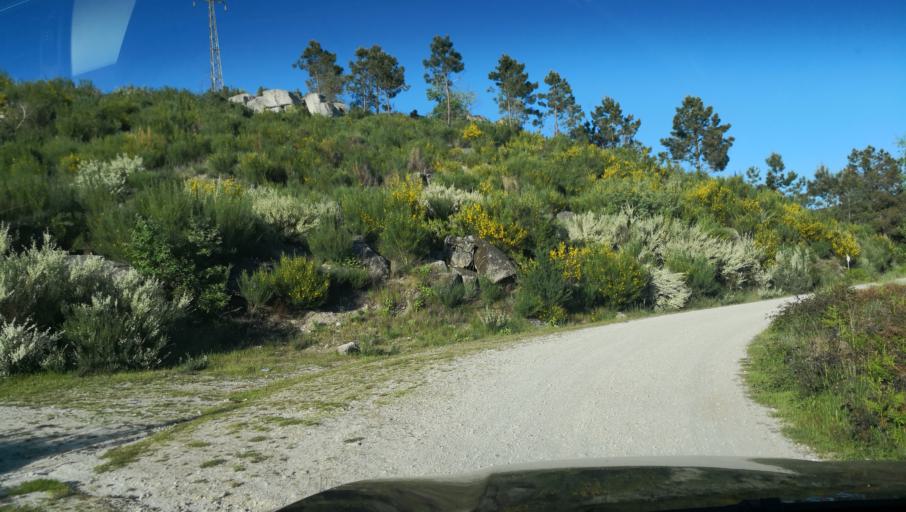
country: PT
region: Vila Real
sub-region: Vila Real
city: Vila Real
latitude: 41.3329
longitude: -7.6762
